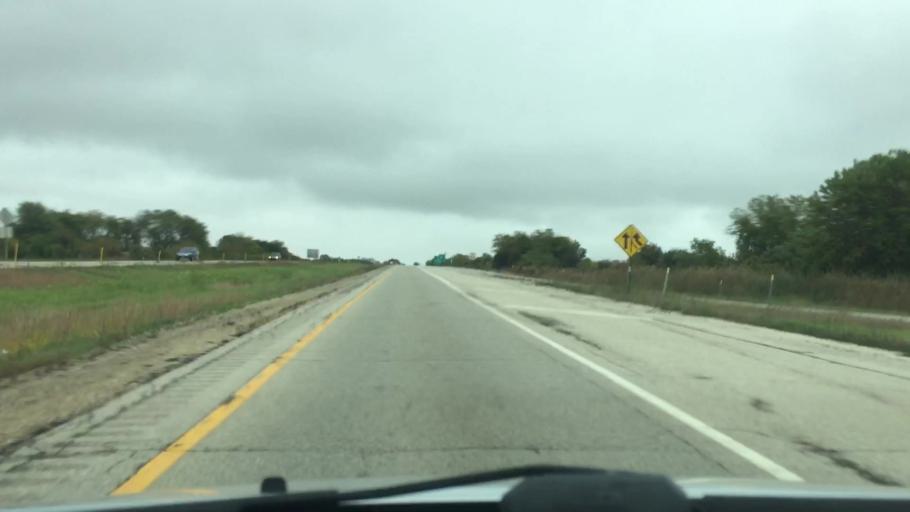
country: US
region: Wisconsin
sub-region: Walworth County
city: Elkhorn
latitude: 42.6959
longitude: -88.5400
